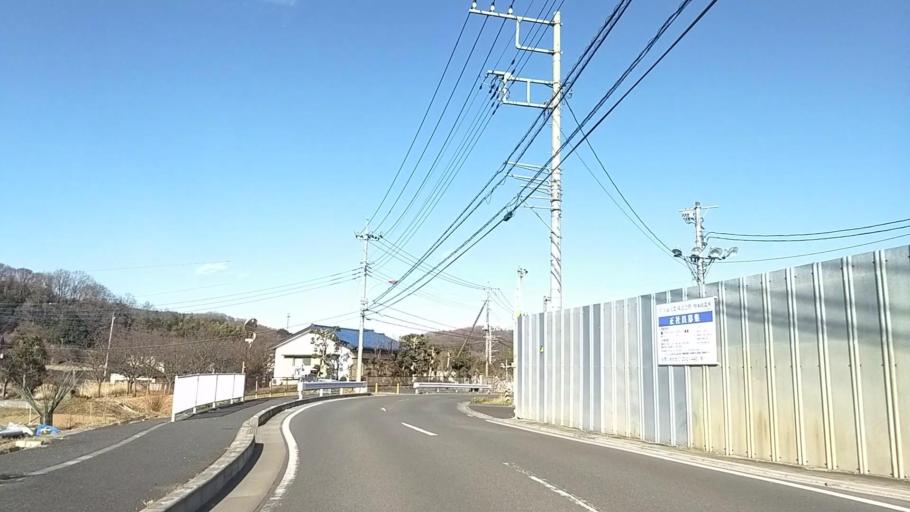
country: JP
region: Kanagawa
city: Atsugi
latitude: 35.4573
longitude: 139.3127
